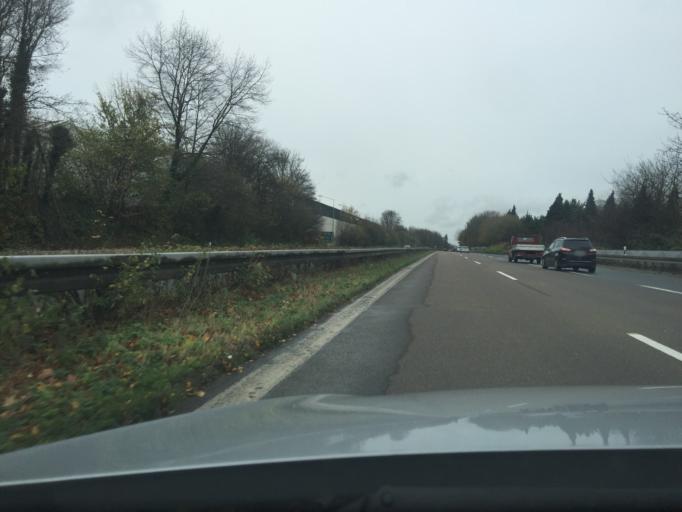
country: DE
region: North Rhine-Westphalia
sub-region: Regierungsbezirk Dusseldorf
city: Velbert
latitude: 51.3405
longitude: 7.0576
